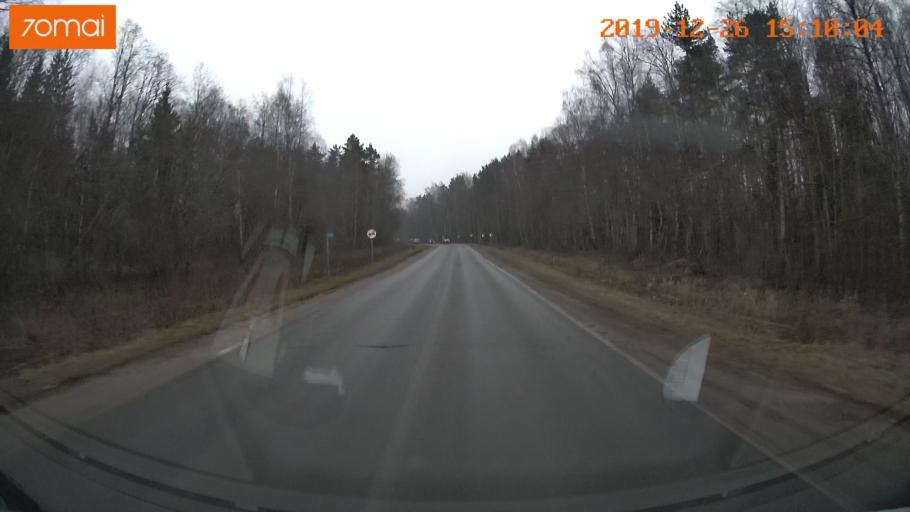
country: RU
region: Jaroslavl
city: Rybinsk
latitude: 58.1434
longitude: 38.8473
